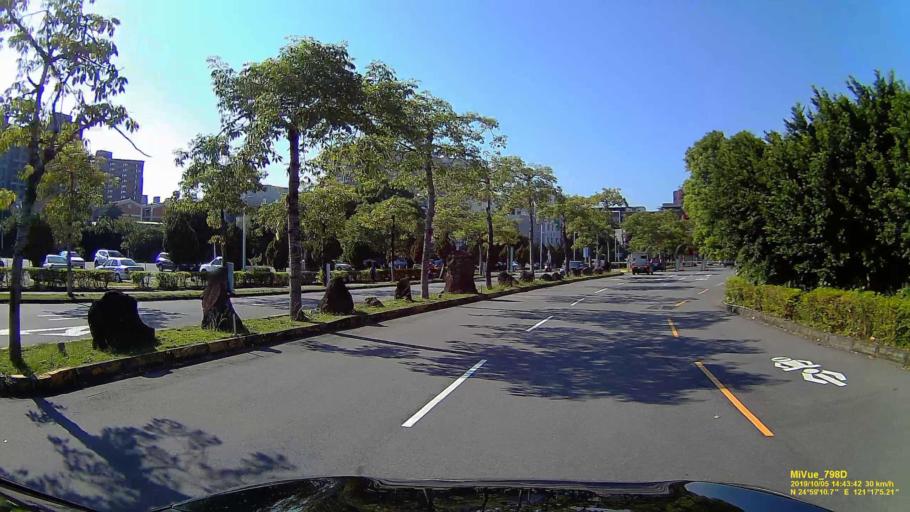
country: TW
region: Taiwan
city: Taoyuan City
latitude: 24.9864
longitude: 121.2846
